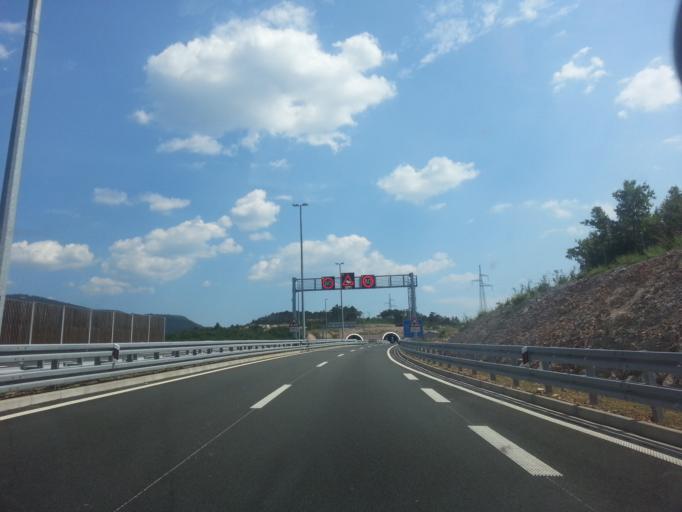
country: HR
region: Primorsko-Goranska
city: Hreljin
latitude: 45.2869
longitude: 14.5866
